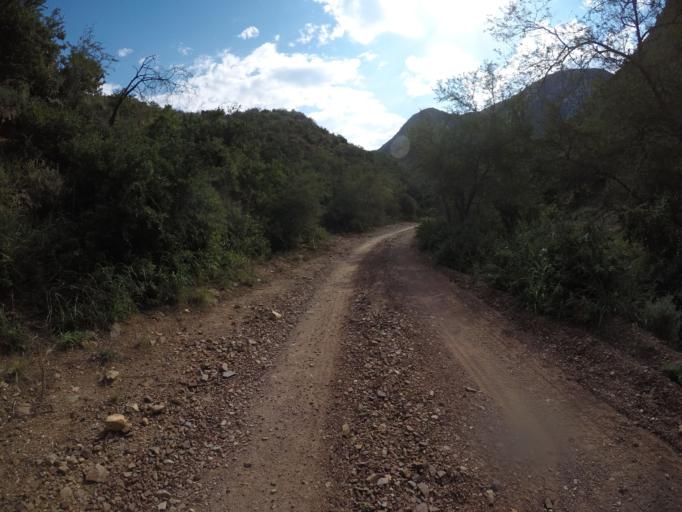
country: ZA
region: Eastern Cape
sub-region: Cacadu District Municipality
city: Kareedouw
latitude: -33.6389
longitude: 24.3230
